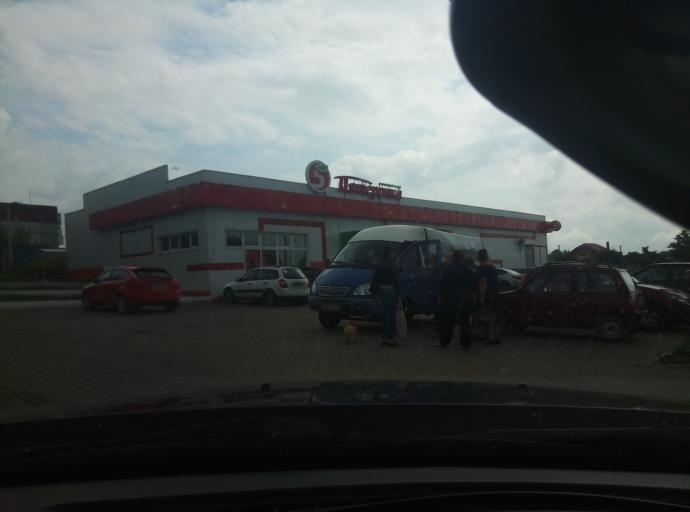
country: RU
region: Tula
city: Bolokhovo
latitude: 54.0821
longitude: 37.8302
